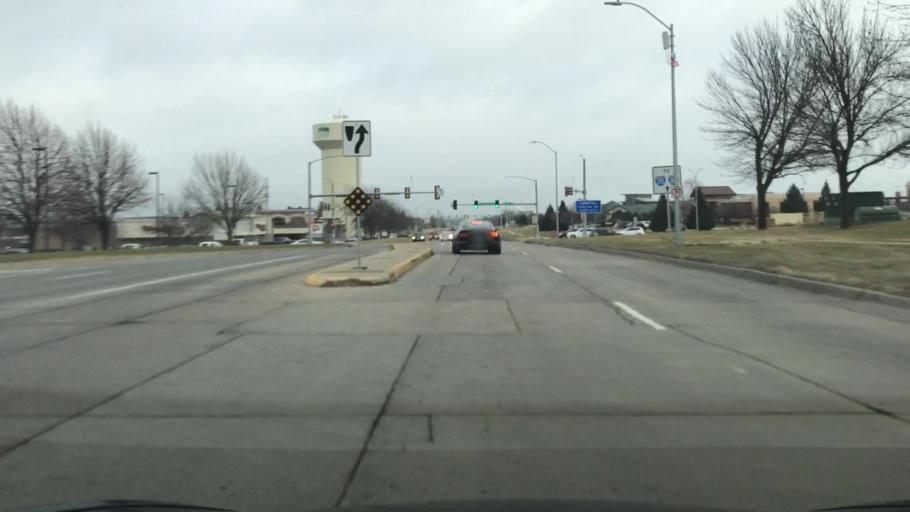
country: US
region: Iowa
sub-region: Polk County
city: Clive
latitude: 41.6005
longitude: -93.7956
